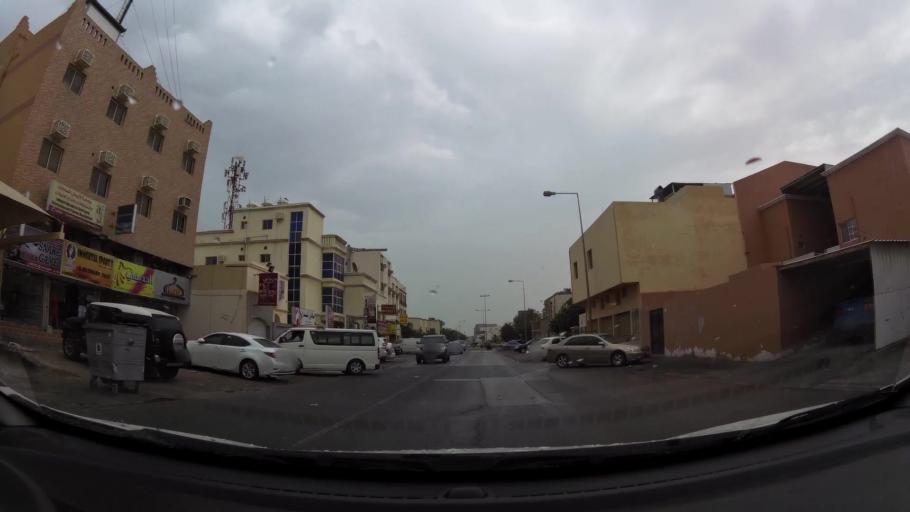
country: BH
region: Northern
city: Madinat `Isa
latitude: 26.1617
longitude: 50.5731
